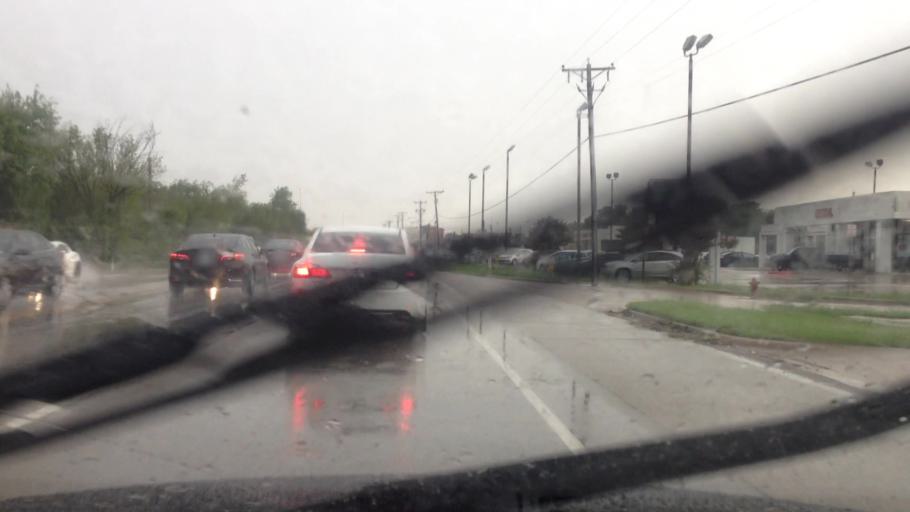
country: US
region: Texas
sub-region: Tarrant County
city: North Richland Hills
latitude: 32.8391
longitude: -97.2075
